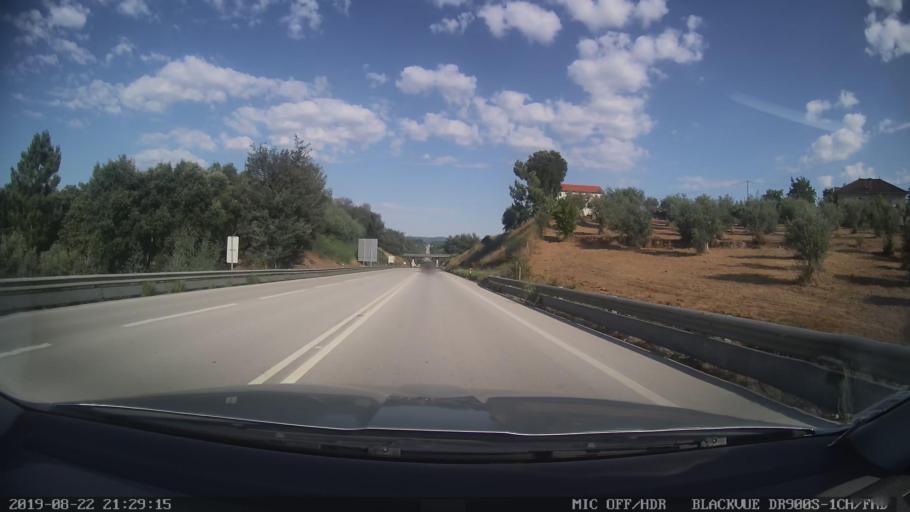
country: PT
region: Leiria
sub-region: Pedrogao Grande
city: Pedrogao Grande
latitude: 39.9010
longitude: -8.1324
